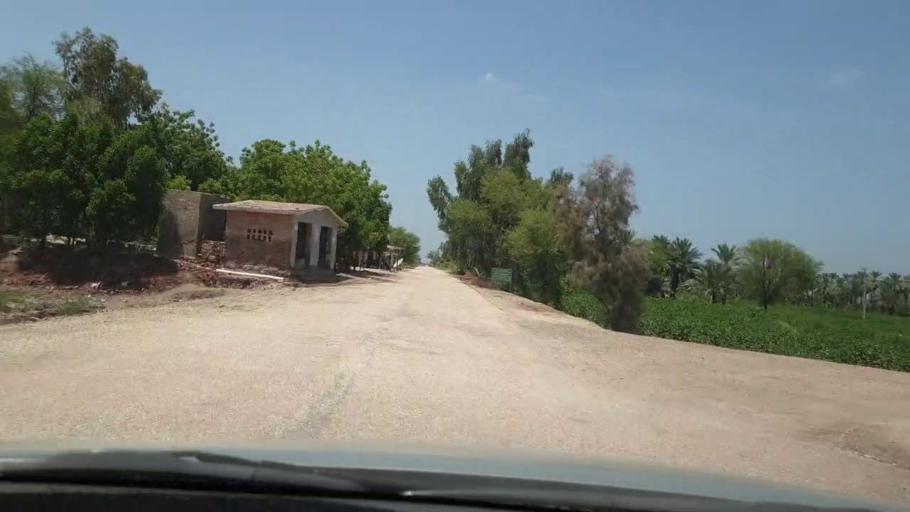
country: PK
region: Sindh
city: Pano Aqil
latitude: 27.7084
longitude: 69.2166
